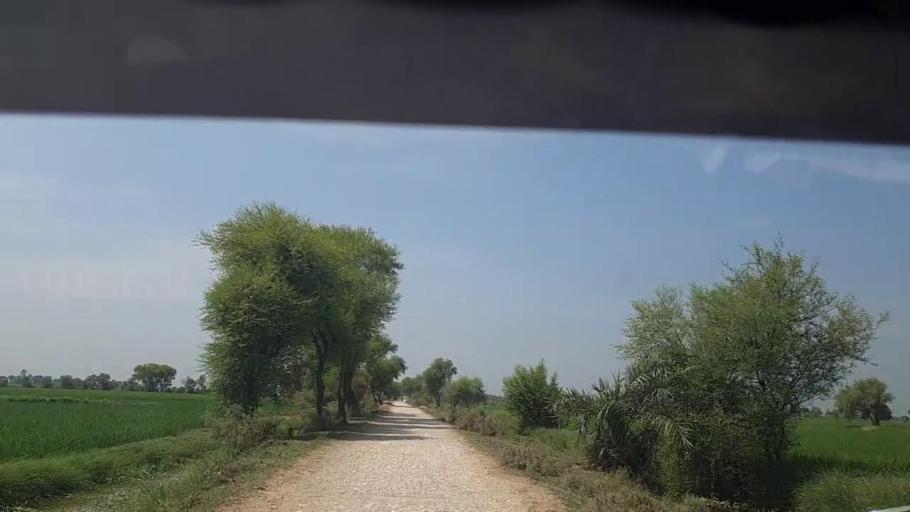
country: PK
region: Sindh
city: Thul
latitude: 28.2047
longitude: 68.6952
